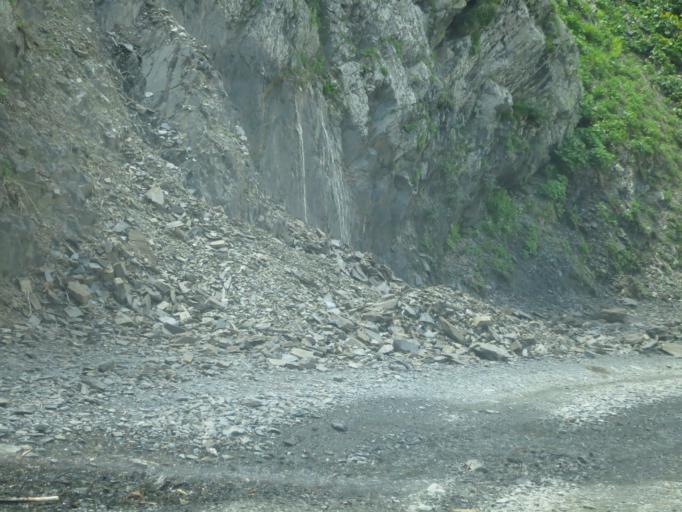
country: GE
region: Kakheti
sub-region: Telavi
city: Telavi
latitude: 42.2602
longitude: 45.5033
